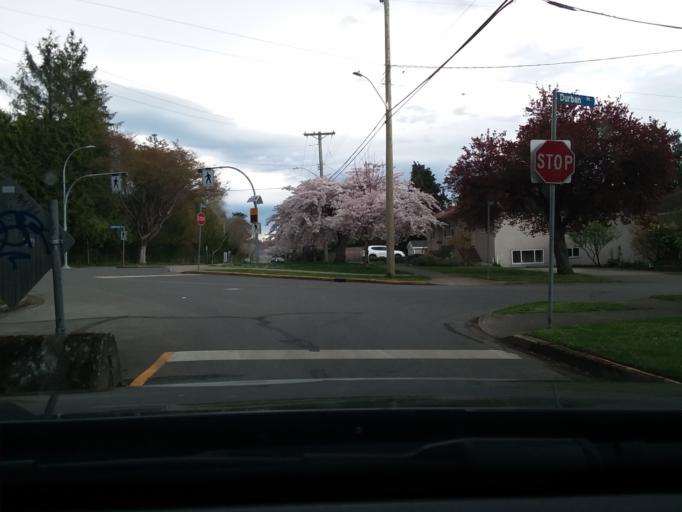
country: CA
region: British Columbia
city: Victoria
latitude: 48.4168
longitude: -123.3455
